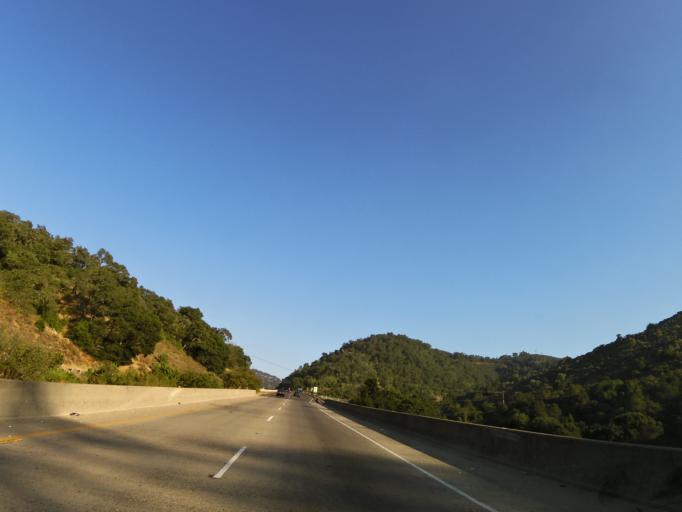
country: US
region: California
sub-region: San Luis Obispo County
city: Santa Margarita
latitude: 35.3537
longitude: -120.6356
